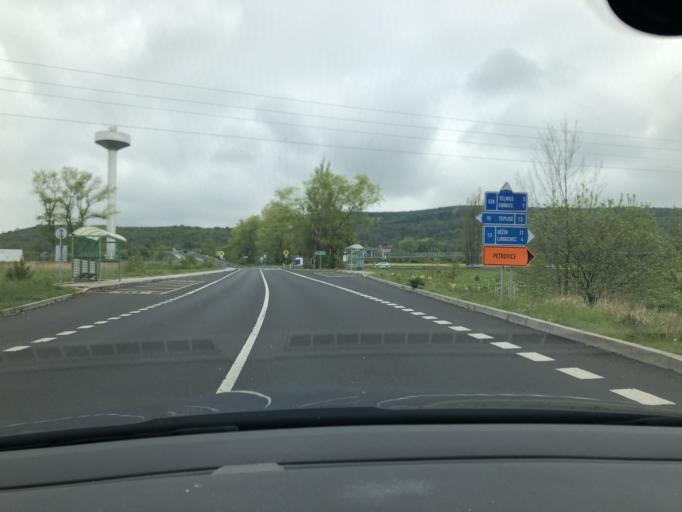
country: CZ
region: Ustecky
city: Libouchec
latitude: 50.7294
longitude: 14.0105
